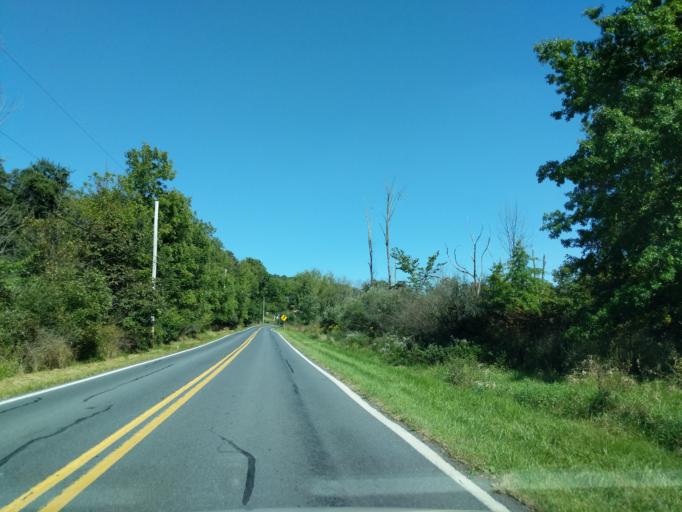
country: US
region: Pennsylvania
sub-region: Bucks County
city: Spinnerstown
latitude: 40.4582
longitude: -75.4847
